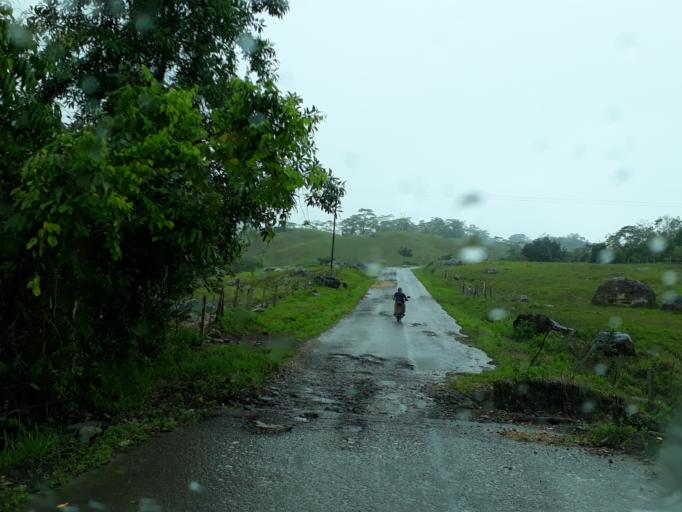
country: CO
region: Cundinamarca
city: Medina
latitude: 4.6698
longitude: -73.3252
